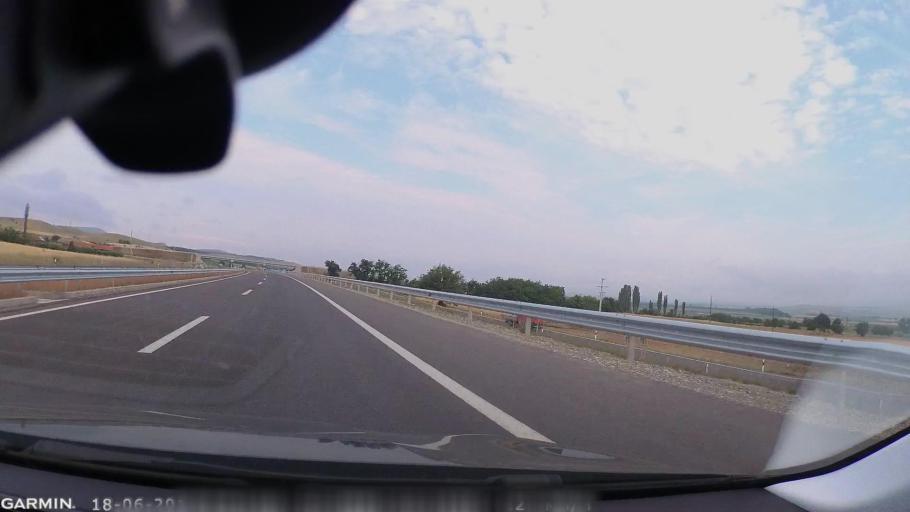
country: MK
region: Stip
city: Shtip
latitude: 41.7896
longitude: 22.1100
